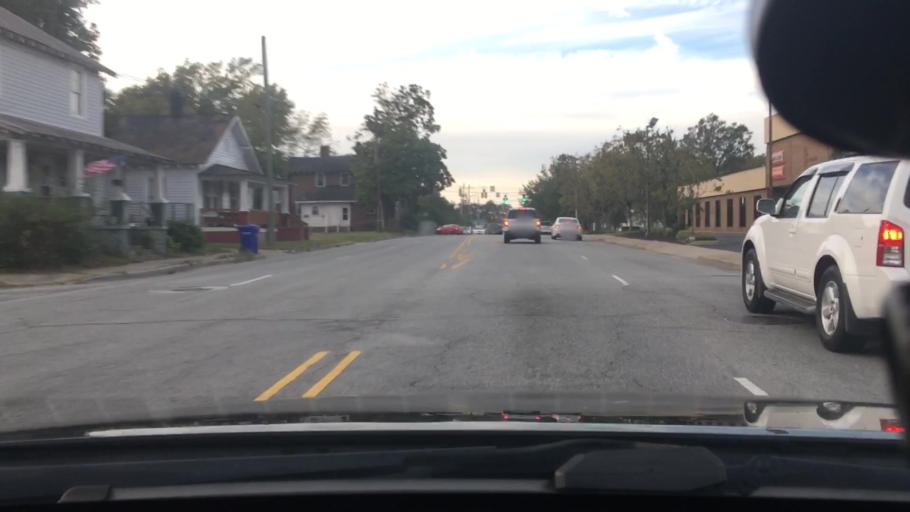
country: US
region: North Carolina
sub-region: Pitt County
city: Greenville
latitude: 35.6046
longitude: -77.3826
